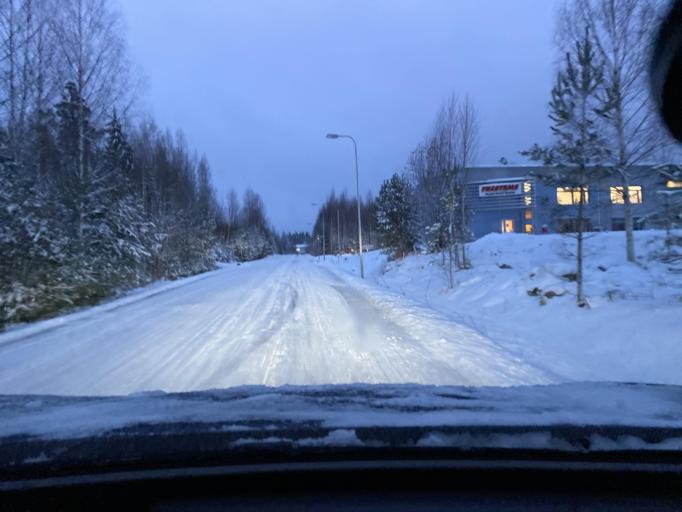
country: FI
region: Pirkanmaa
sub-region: Lounais-Pirkanmaa
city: Vammala
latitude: 61.3127
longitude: 22.9290
